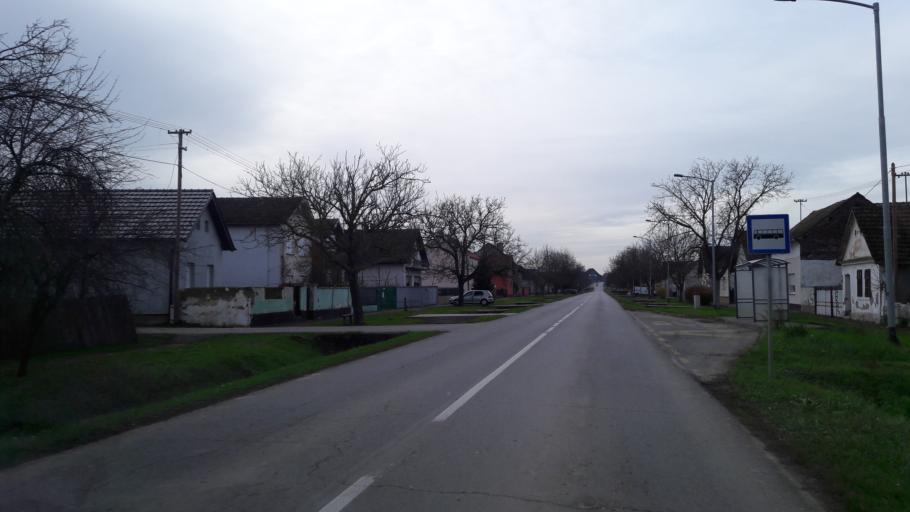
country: HR
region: Osjecko-Baranjska
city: Semeljci
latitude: 45.3653
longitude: 18.5461
